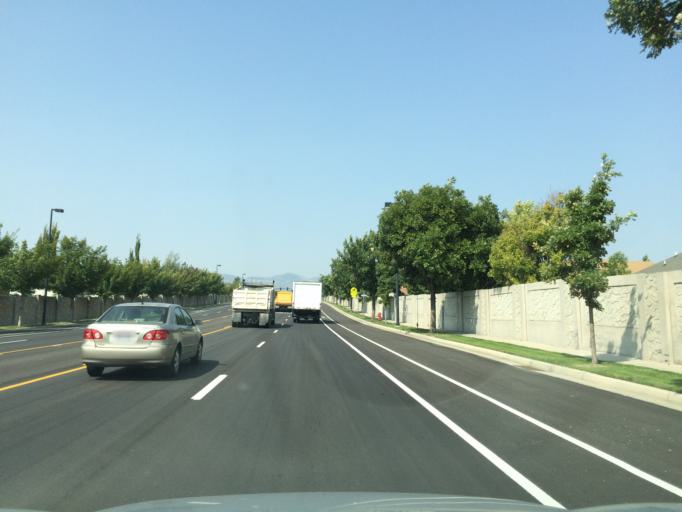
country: US
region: Utah
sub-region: Salt Lake County
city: Oquirrh
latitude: 40.5879
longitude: -112.0110
